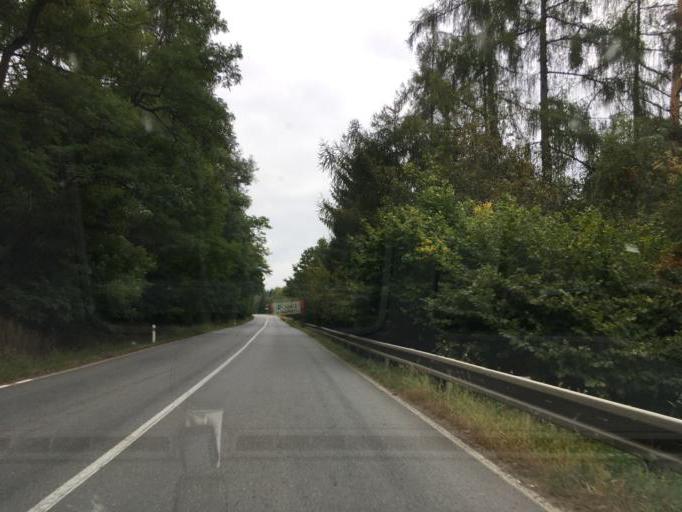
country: CZ
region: Vysocina
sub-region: Okres Pelhrimov
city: Zeliv
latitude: 49.5534
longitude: 15.1298
